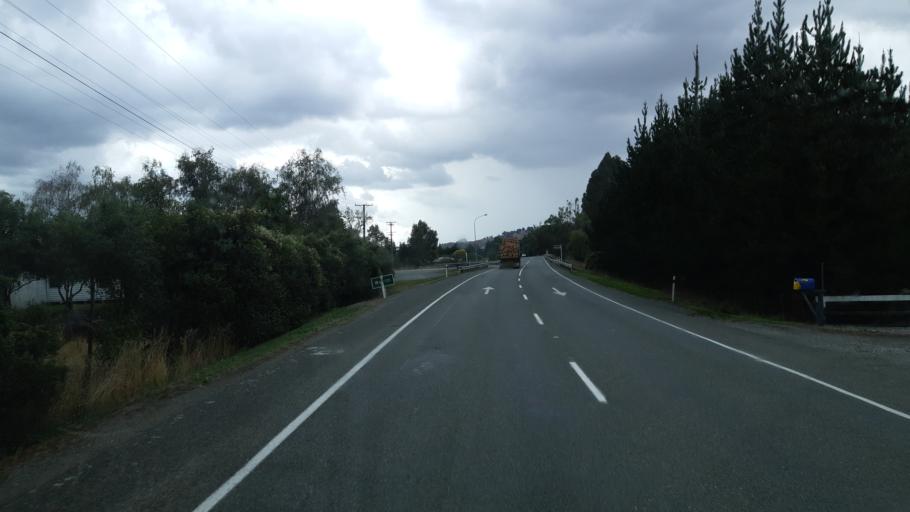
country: NZ
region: Tasman
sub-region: Tasman District
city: Wakefield
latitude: -41.4290
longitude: 172.9881
